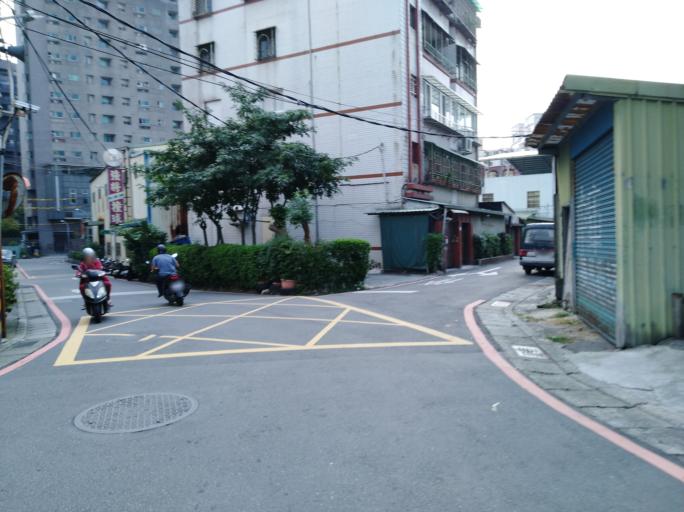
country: TW
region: Taipei
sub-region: Taipei
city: Banqiao
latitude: 25.0429
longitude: 121.4256
